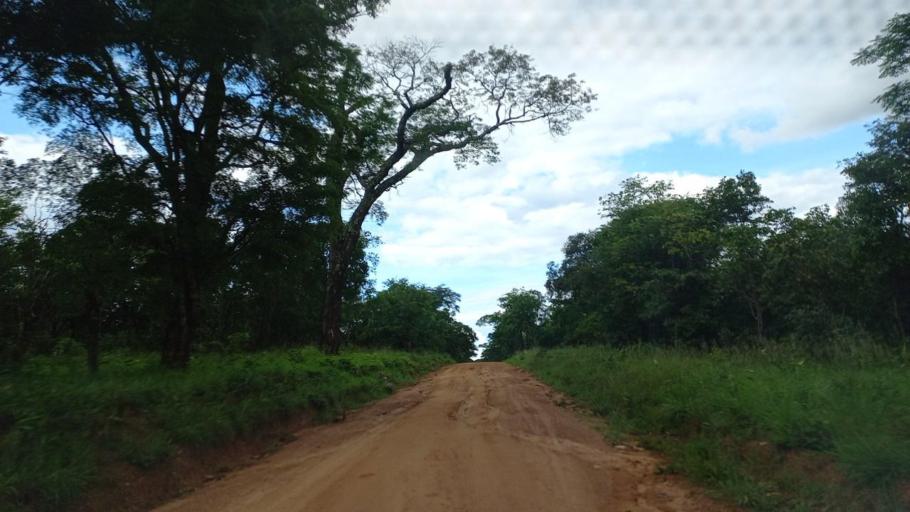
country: ZM
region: North-Western
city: Mwinilunga
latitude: -11.8364
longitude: 24.3675
